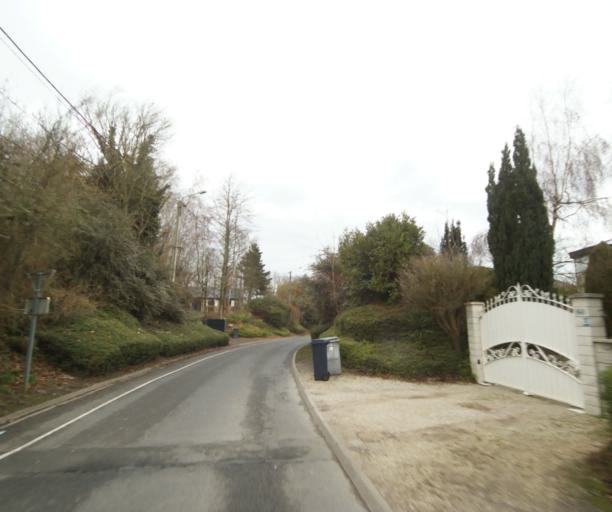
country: FR
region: Nord-Pas-de-Calais
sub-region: Departement du Nord
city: Saint-Saulve
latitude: 50.3615
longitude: 3.5660
